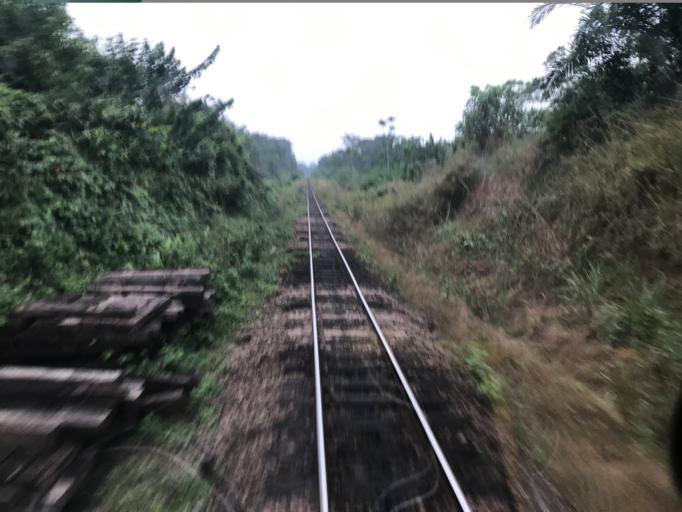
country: CM
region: Littoral
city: Edea
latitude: 3.9369
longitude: 10.0988
